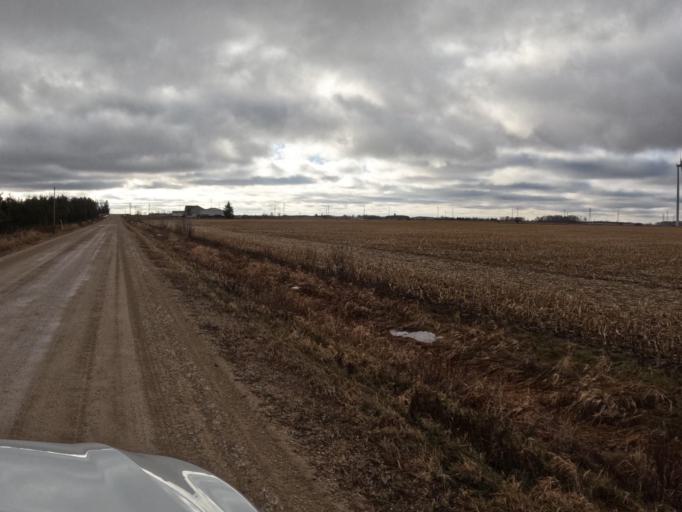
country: CA
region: Ontario
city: Shelburne
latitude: 44.0073
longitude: -80.3887
